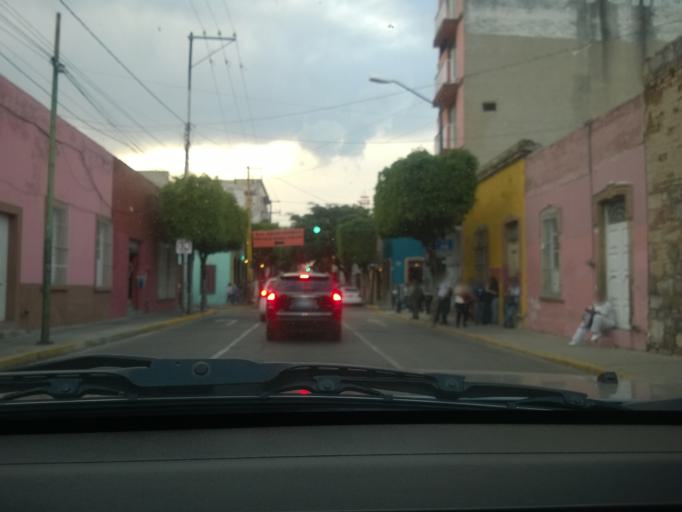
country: MX
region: Guanajuato
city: Leon
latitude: 21.1220
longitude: -101.6766
